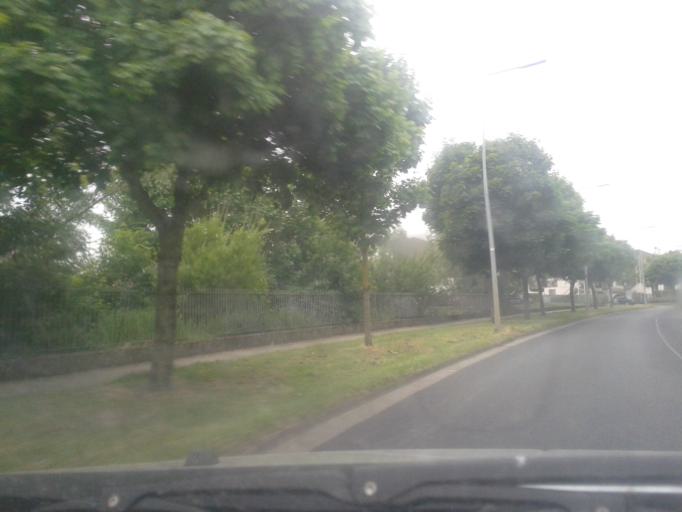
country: IE
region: Leinster
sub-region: Dublin City
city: Finglas
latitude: 53.3990
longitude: -6.2871
